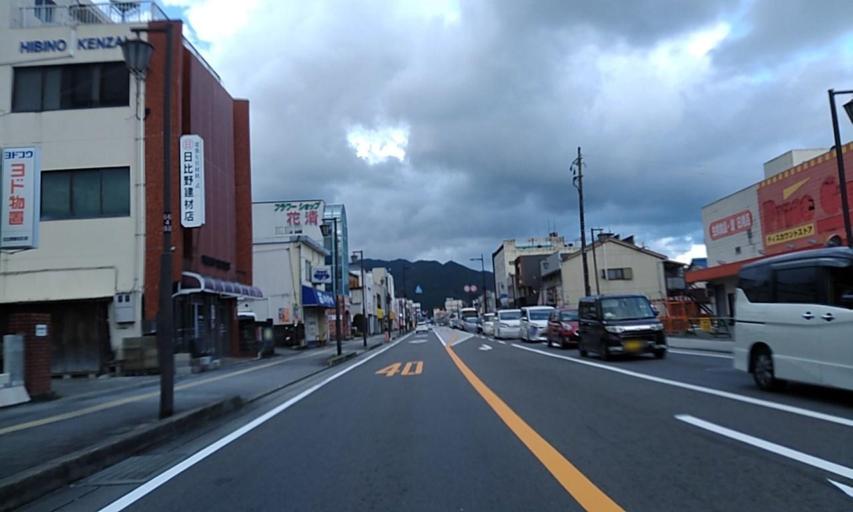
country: JP
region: Wakayama
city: Shingu
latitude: 33.7222
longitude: 135.9865
